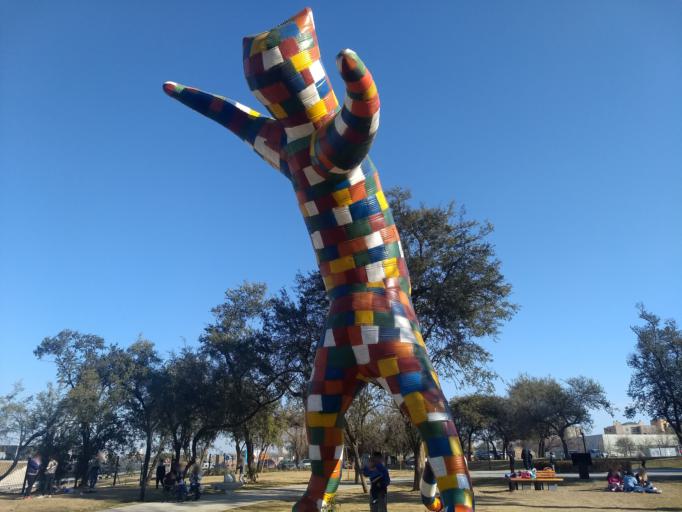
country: AR
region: Cordoba
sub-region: Departamento de Capital
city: Cordoba
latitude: -31.3751
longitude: -64.2551
